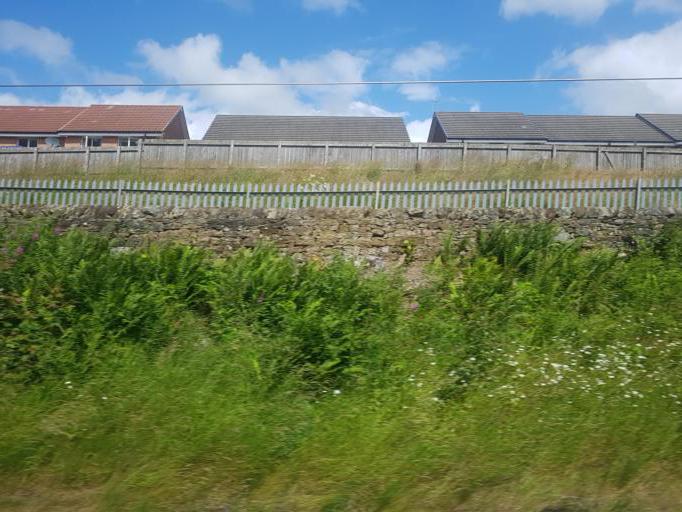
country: GB
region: Scotland
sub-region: Falkirk
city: Falkirk
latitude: 55.9840
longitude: -3.7536
